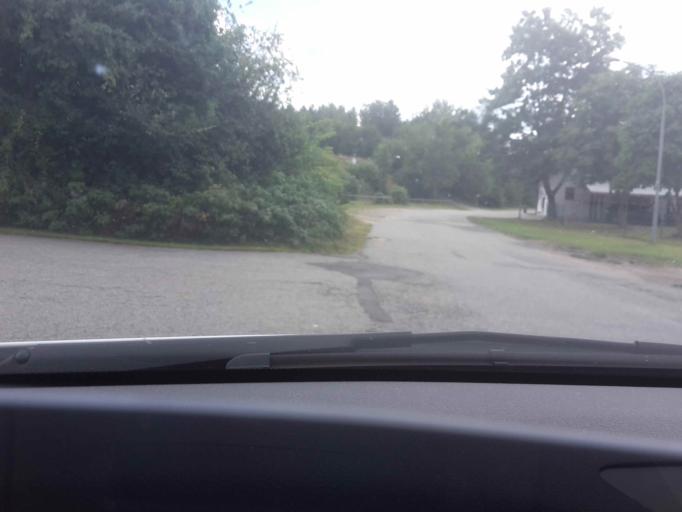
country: DE
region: Bavaria
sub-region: Lower Bavaria
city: Zwiesel
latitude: 49.0241
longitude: 13.2442
